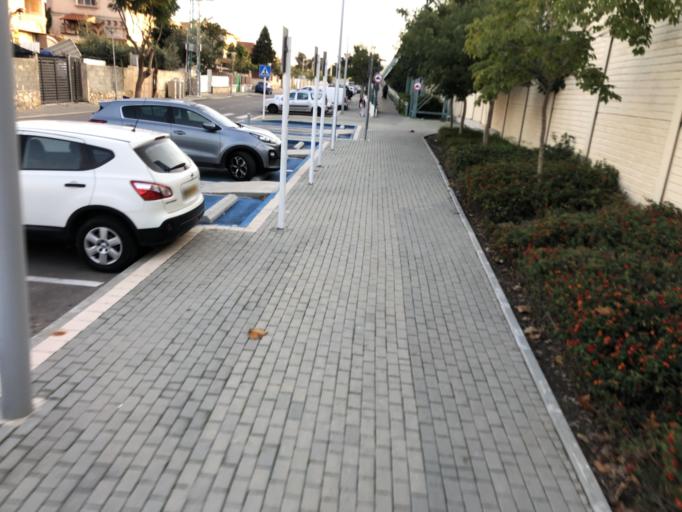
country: IL
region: Northern District
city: `Akko
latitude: 32.9273
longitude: 35.0837
